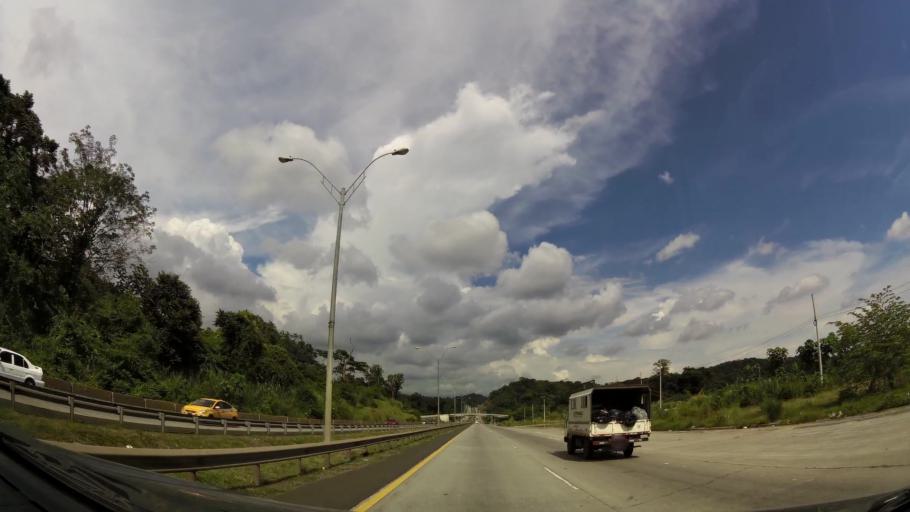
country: PA
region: Panama
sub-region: Distrito de Panama
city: Paraiso
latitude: 9.0330
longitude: -79.5808
